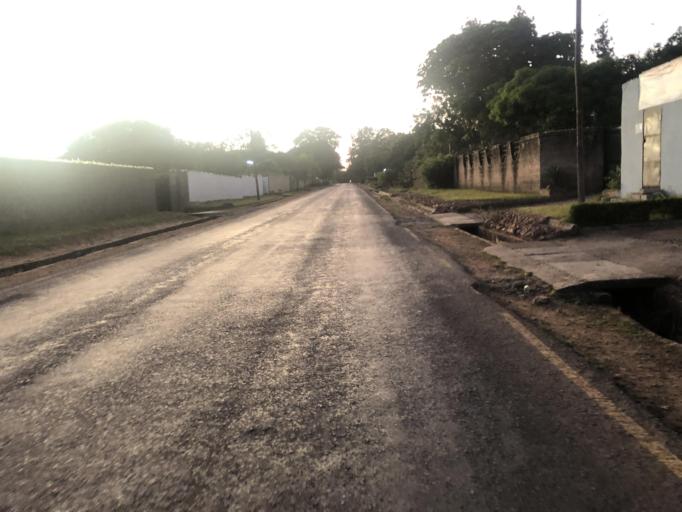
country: ZM
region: Lusaka
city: Lusaka
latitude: -15.3889
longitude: 28.3371
